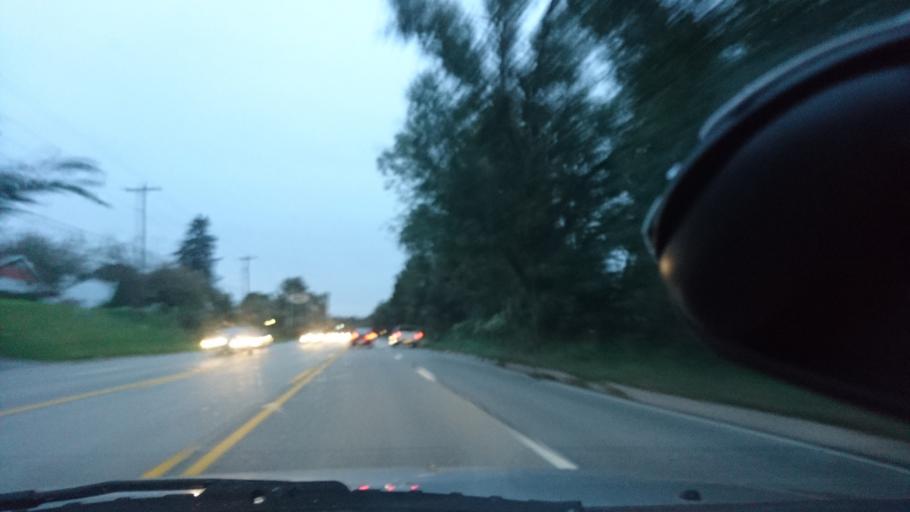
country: US
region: Pennsylvania
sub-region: Delaware County
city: Media
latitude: 39.8913
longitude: -75.4038
